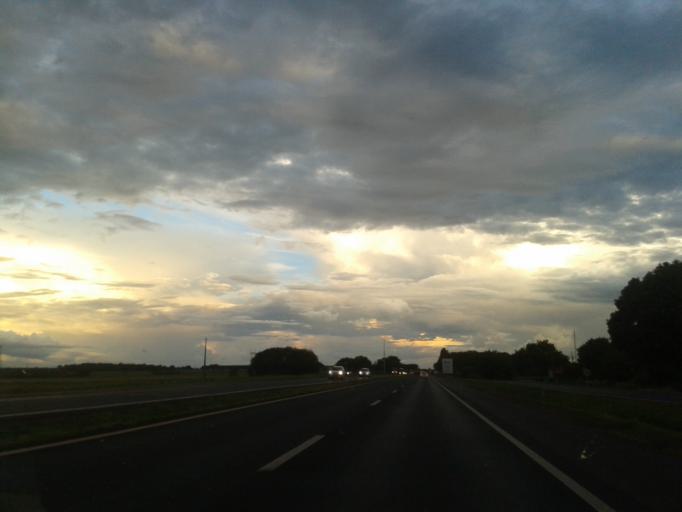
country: BR
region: Minas Gerais
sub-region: Centralina
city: Centralina
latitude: -18.7164
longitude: -49.1296
